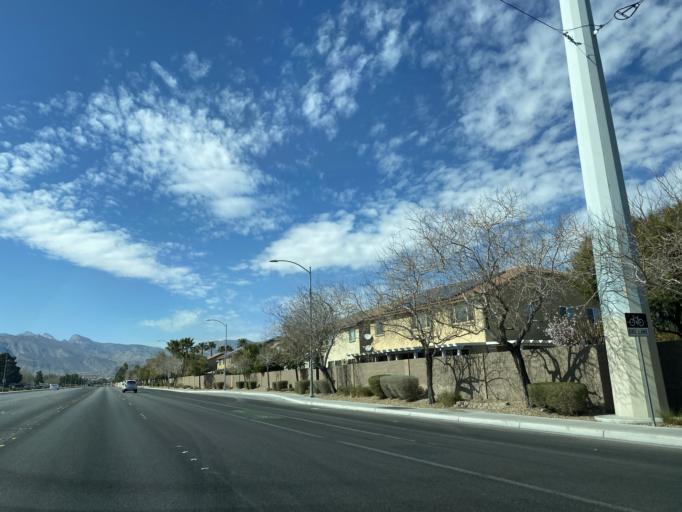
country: US
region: Nevada
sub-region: Clark County
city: Spring Valley
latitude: 36.2331
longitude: -115.2517
